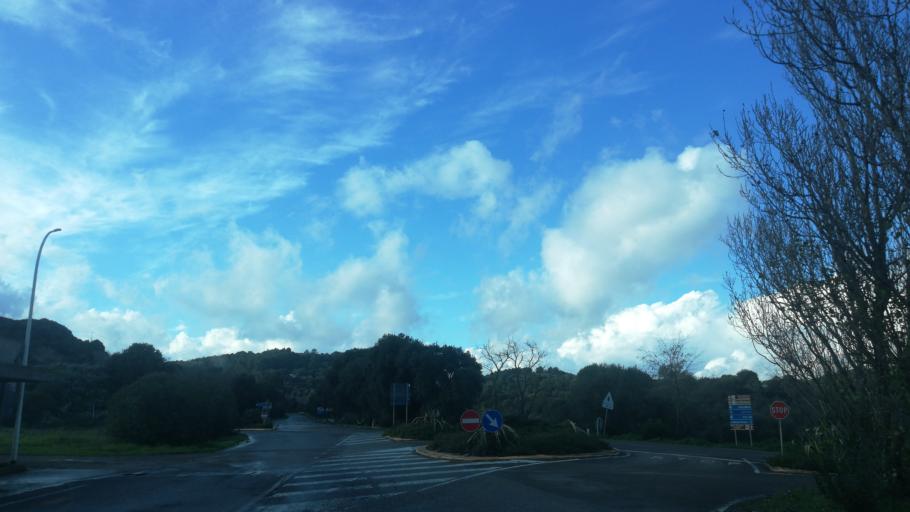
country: IT
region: Sardinia
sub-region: Provincia di Medio Campidano
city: Villanovaforru
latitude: 39.6331
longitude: 8.8643
